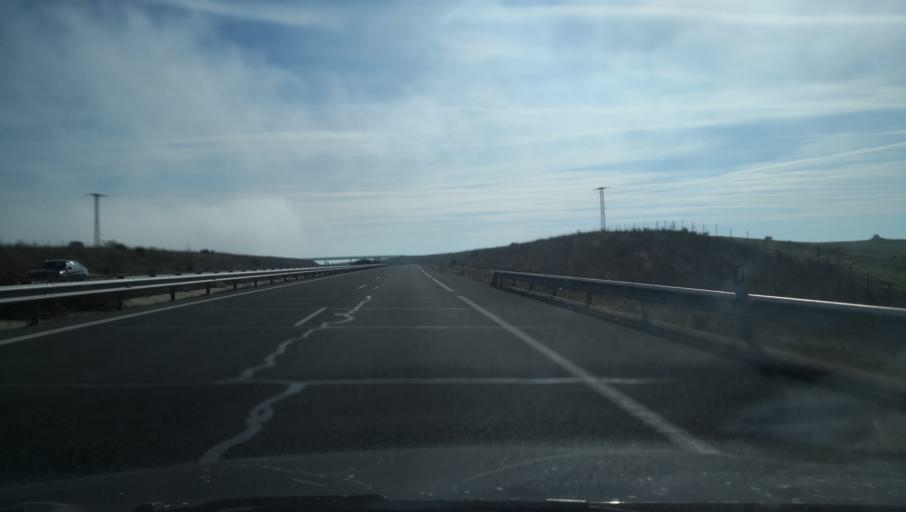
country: ES
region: Castille and Leon
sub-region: Provincia de Salamanca
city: Machacon
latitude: 40.9248
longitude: -5.5361
